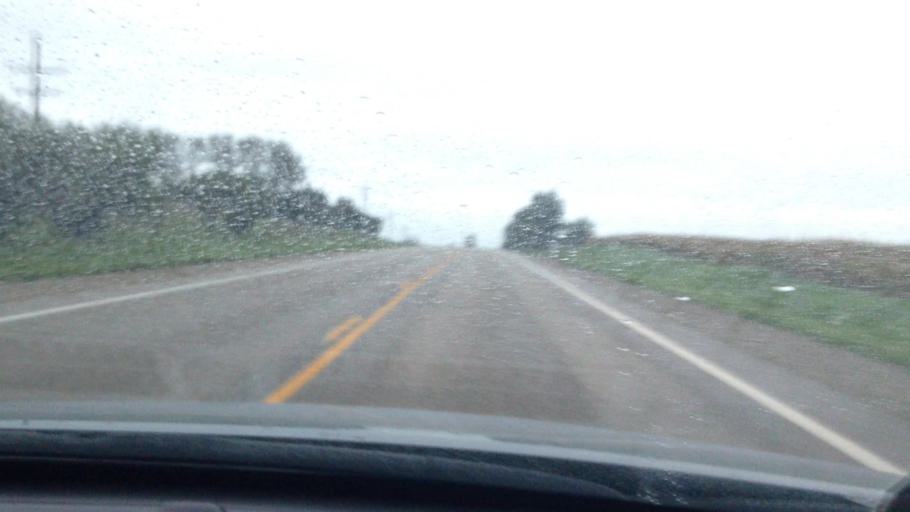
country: US
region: Kansas
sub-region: Brown County
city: Hiawatha
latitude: 39.8180
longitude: -95.5273
